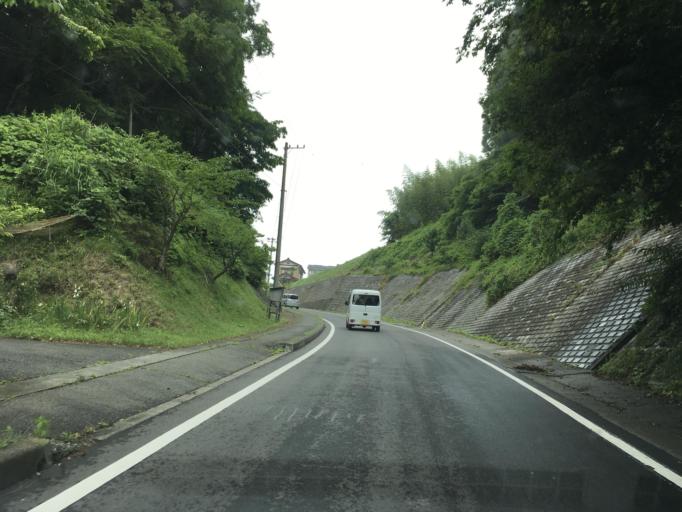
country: JP
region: Iwate
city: Ofunato
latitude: 38.8954
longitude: 141.6407
